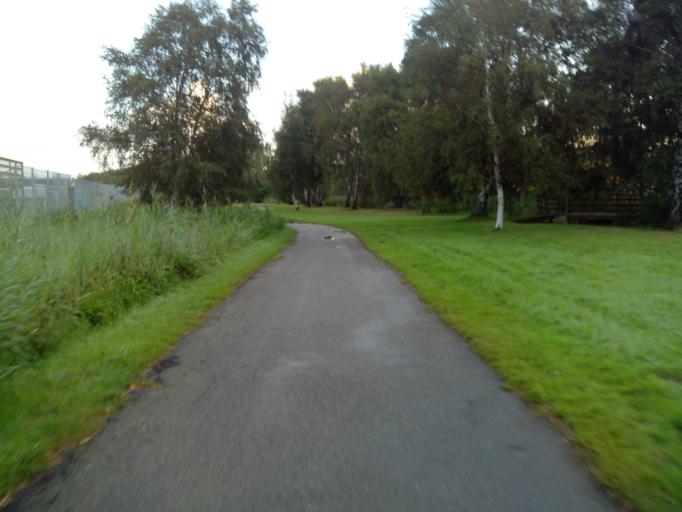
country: SE
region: Vaestra Goetaland
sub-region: Goteborg
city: Goeteborg
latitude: 57.7312
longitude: 11.9527
